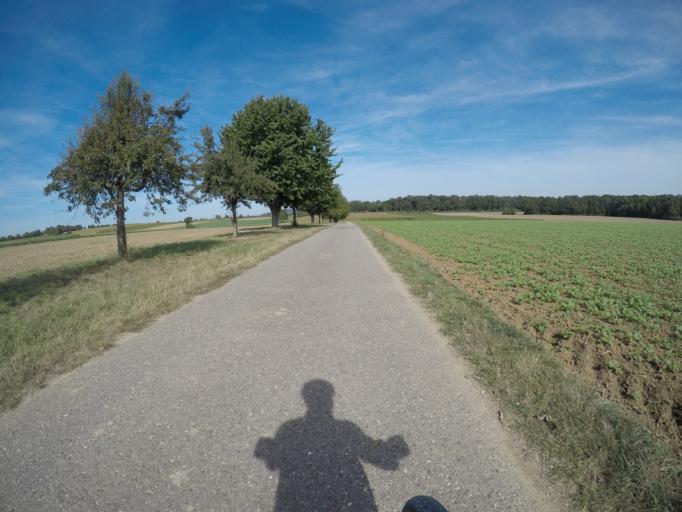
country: DE
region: Baden-Wuerttemberg
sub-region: Regierungsbezirk Stuttgart
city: Oberriexingen
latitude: 48.9454
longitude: 9.0270
